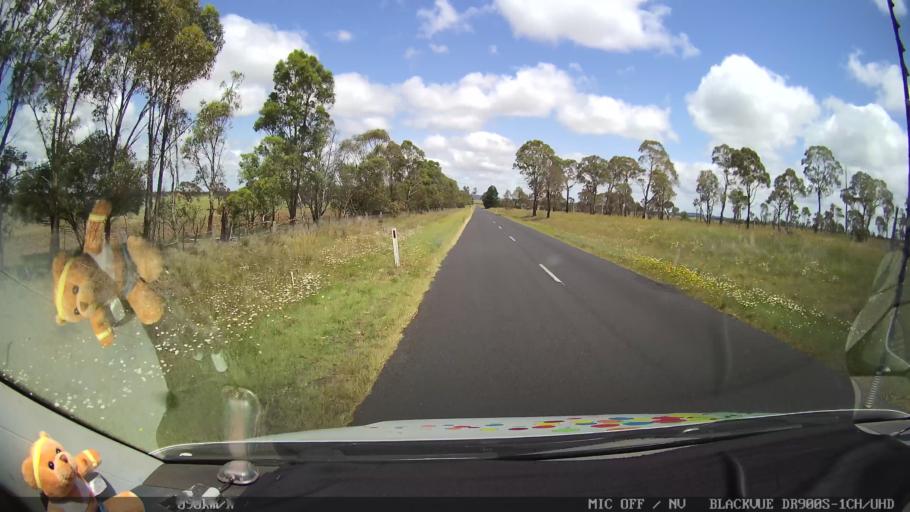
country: AU
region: New South Wales
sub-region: Glen Innes Severn
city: Glen Innes
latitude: -29.6875
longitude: 151.7056
